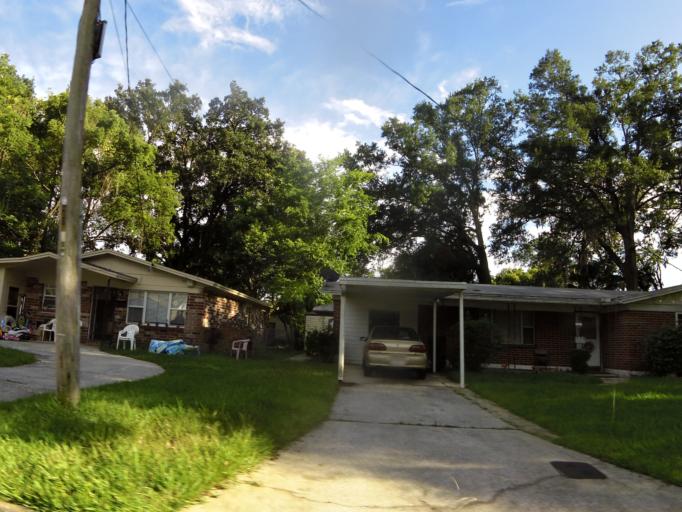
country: US
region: Florida
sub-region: Duval County
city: Jacksonville
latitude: 30.3099
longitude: -81.7292
